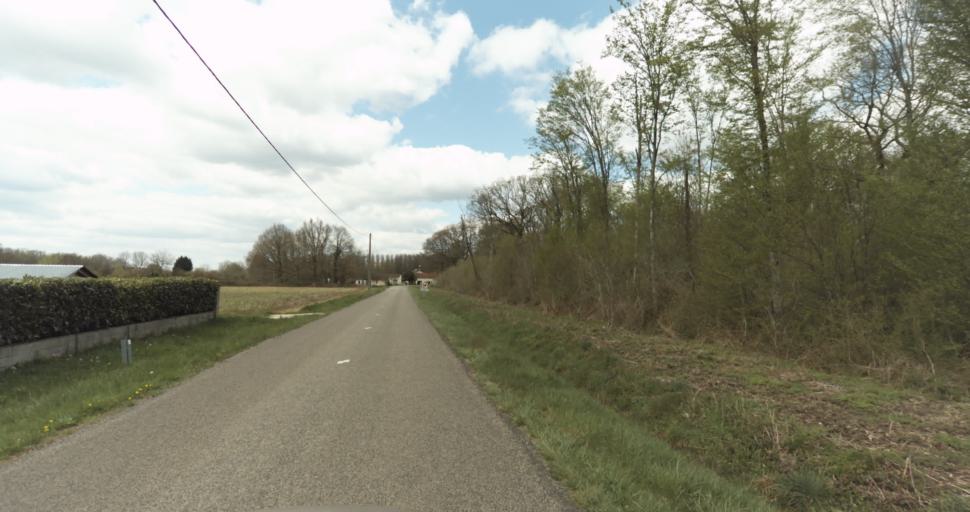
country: FR
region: Bourgogne
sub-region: Departement de la Cote-d'Or
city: Auxonne
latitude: 47.1743
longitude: 5.4245
